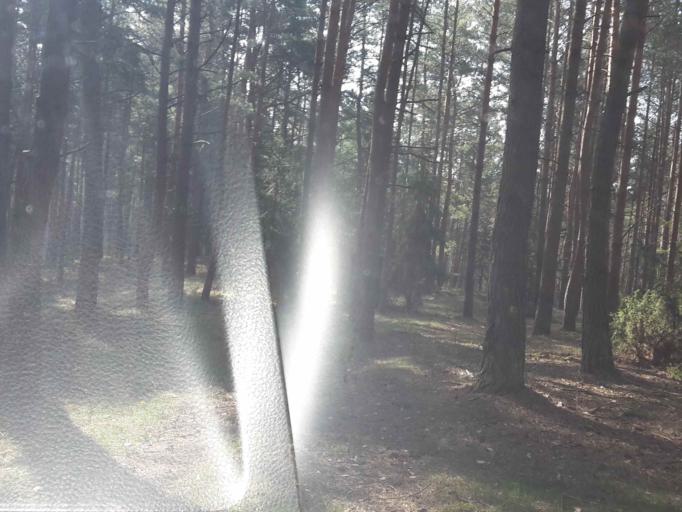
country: PL
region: Kujawsko-Pomorskie
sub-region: Powiat brodnicki
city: Brodnica
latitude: 53.3204
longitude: 19.3615
